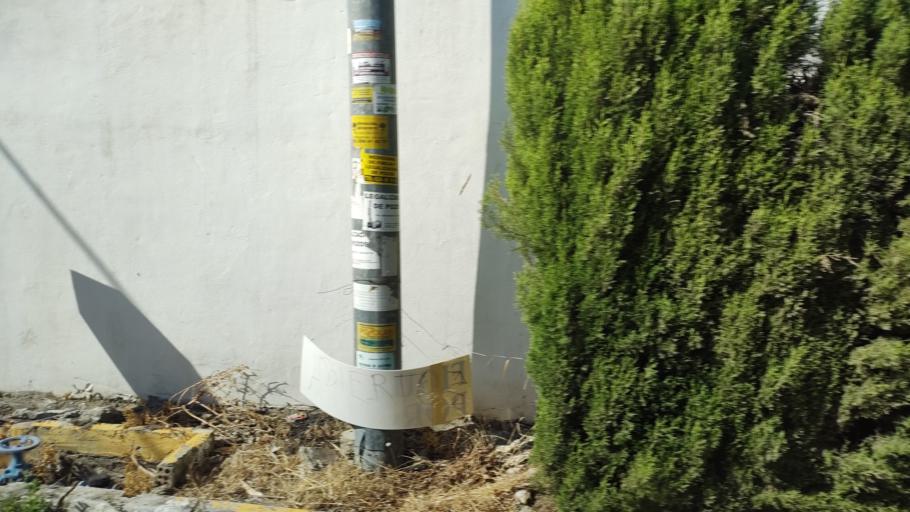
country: ES
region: Andalusia
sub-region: Provincia de Sevilla
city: Aguadulce
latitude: 37.2563
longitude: -4.9858
